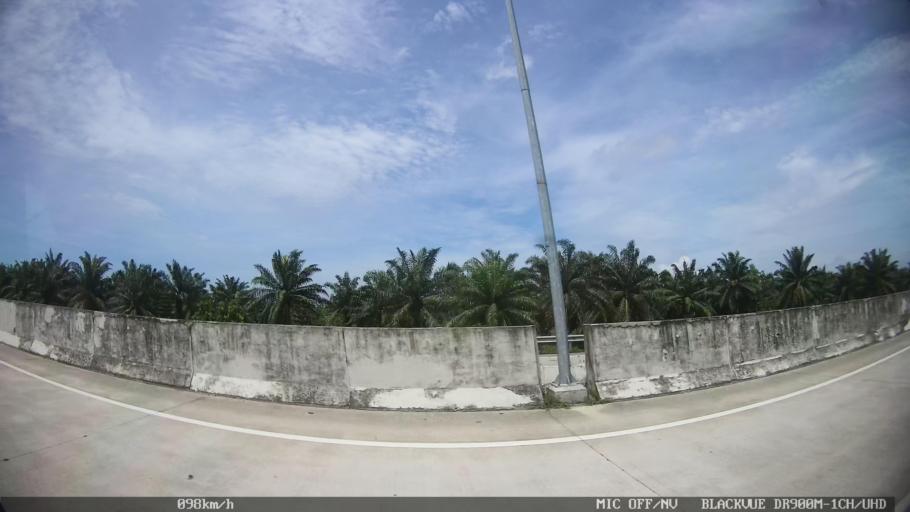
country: ID
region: North Sumatra
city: Percut
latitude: 3.5940
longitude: 98.8439
